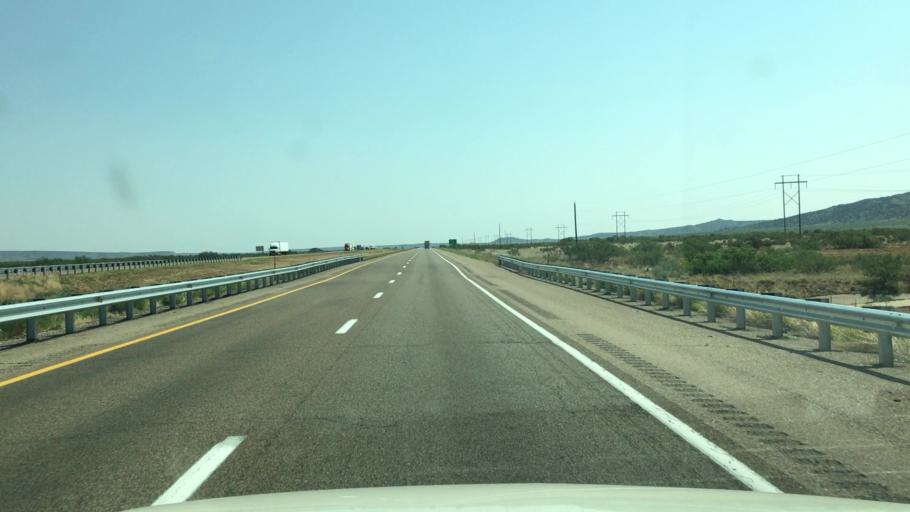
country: US
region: New Mexico
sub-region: Quay County
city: Tucumcari
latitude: 35.1043
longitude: -104.0319
